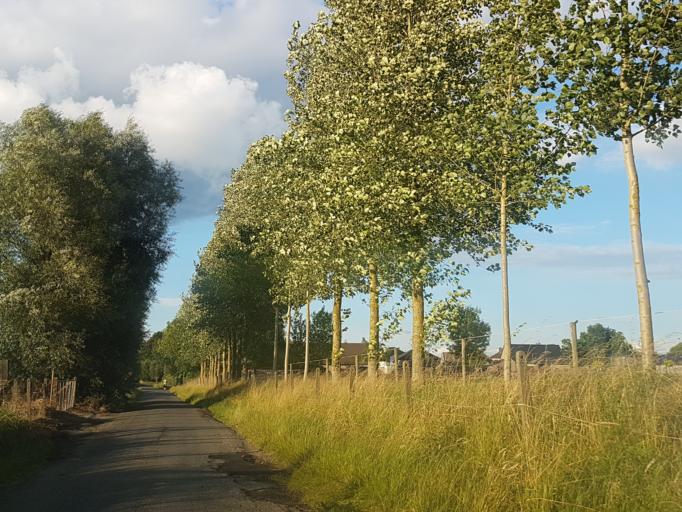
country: BE
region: Flanders
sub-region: Provincie Vlaams-Brabant
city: Opwijk
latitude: 50.9517
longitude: 4.1574
